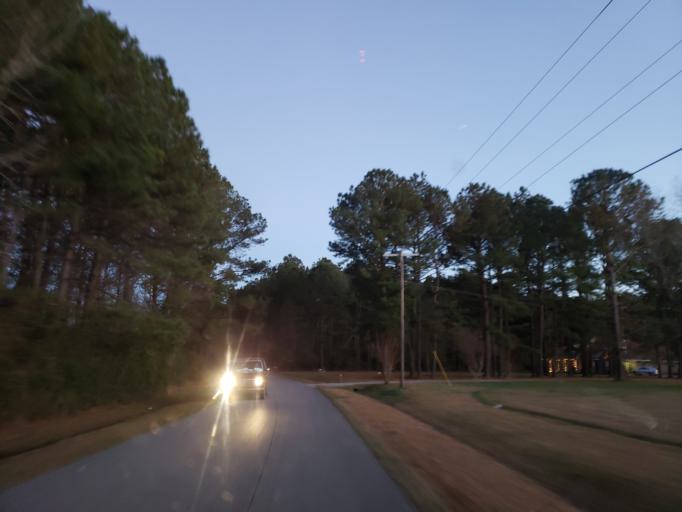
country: US
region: Mississippi
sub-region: Forrest County
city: Rawls Springs
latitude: 31.4395
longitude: -89.3787
